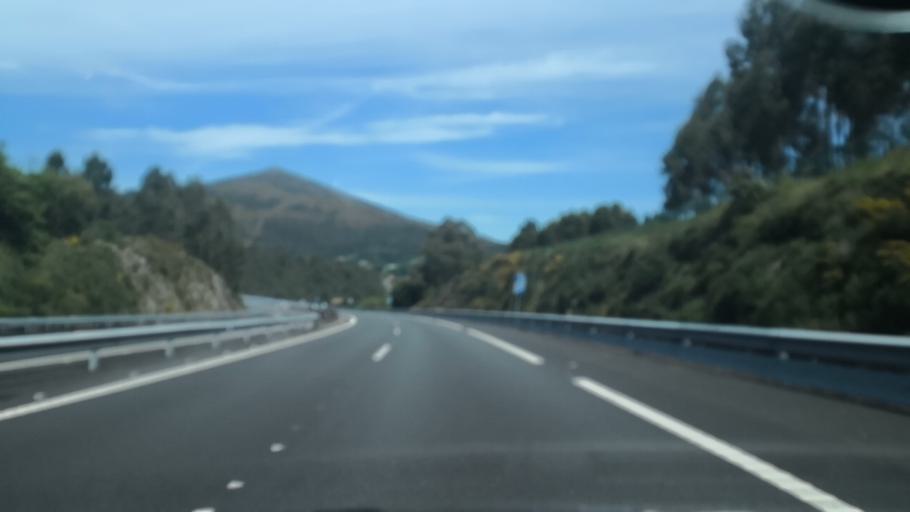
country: ES
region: Galicia
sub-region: Provincia da Coruna
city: Padron
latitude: 42.7275
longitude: -8.6369
